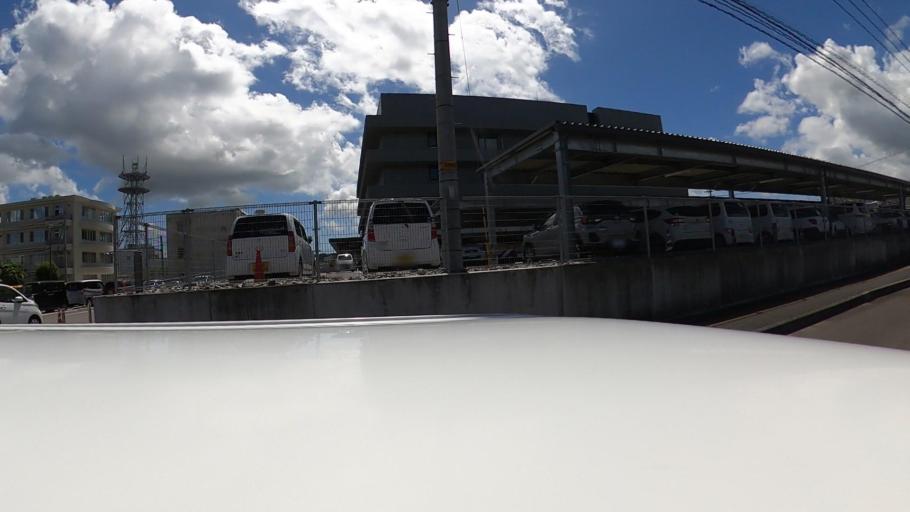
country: JP
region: Miyazaki
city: Tsuma
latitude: 32.1082
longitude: 131.4004
